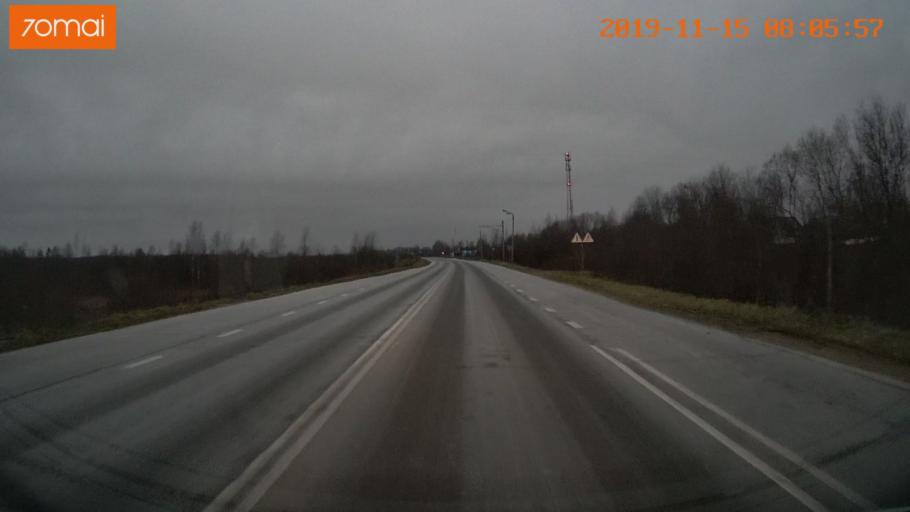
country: RU
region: Vologda
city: Cherepovets
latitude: 59.0199
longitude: 38.0471
